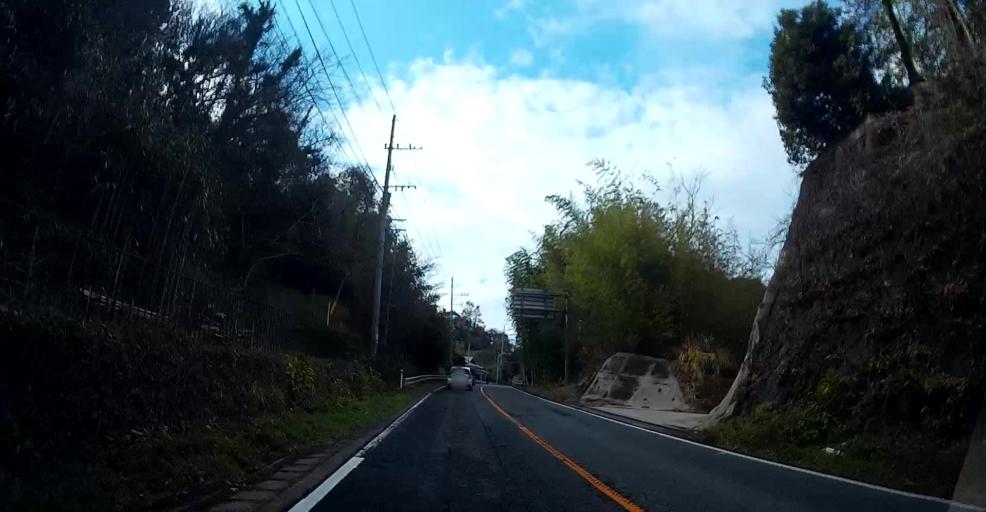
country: JP
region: Kumamoto
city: Yatsushiro
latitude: 32.6090
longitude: 130.4646
